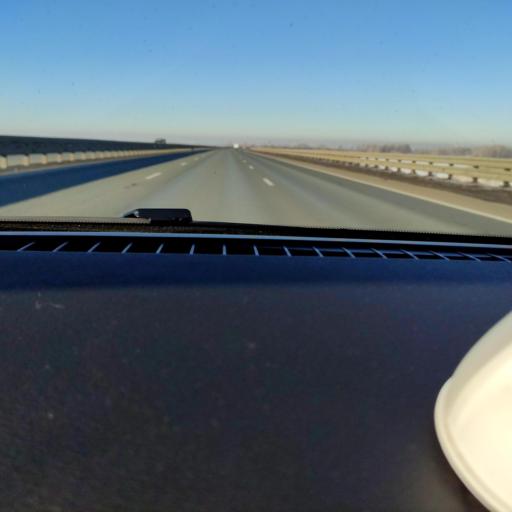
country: RU
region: Samara
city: Smyshlyayevka
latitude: 53.1576
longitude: 50.3364
